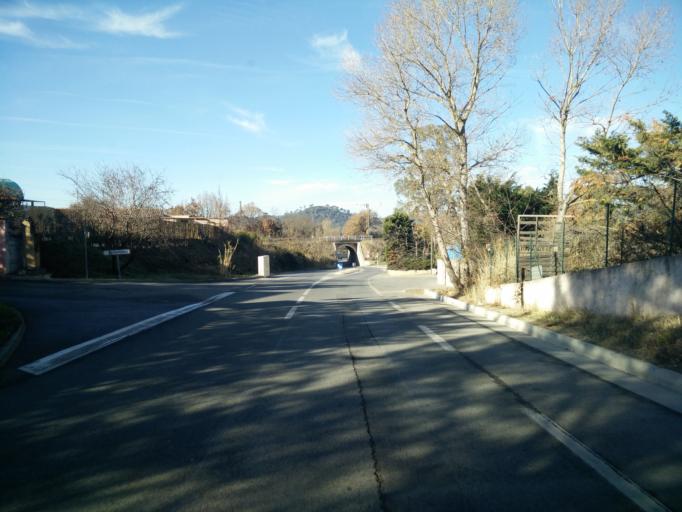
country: FR
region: Provence-Alpes-Cote d'Azur
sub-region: Departement du Var
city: Vidauban
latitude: 43.4147
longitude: 6.4285
